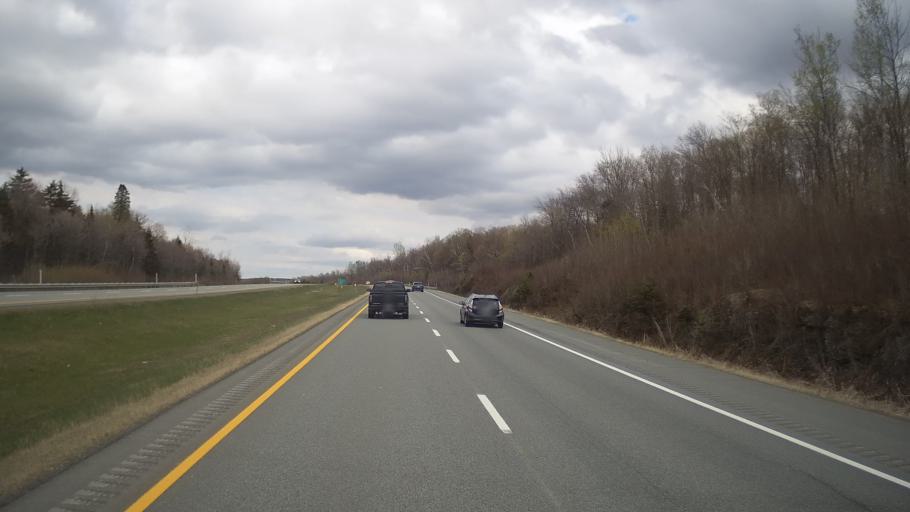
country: CA
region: Quebec
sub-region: Monteregie
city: Waterloo
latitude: 45.3021
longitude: -72.4048
